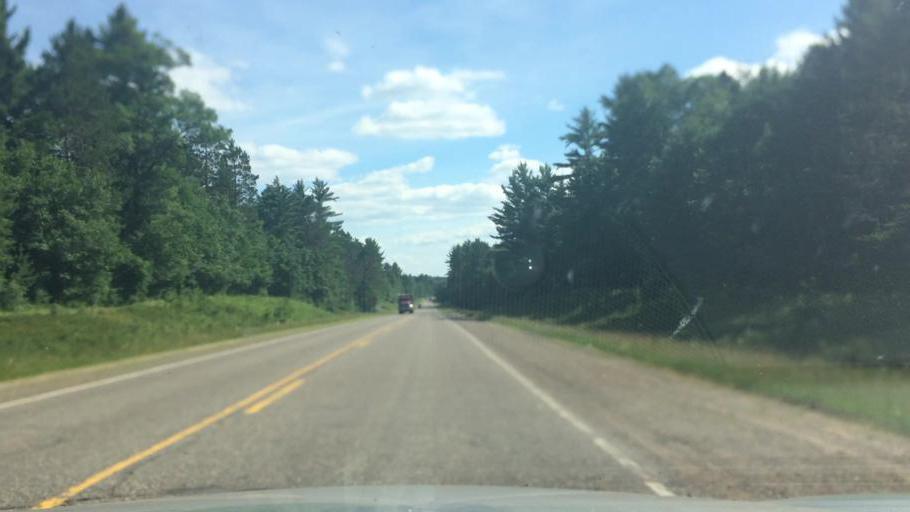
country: US
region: Wisconsin
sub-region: Vilas County
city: Lac du Flambeau
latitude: 46.0733
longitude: -89.6443
